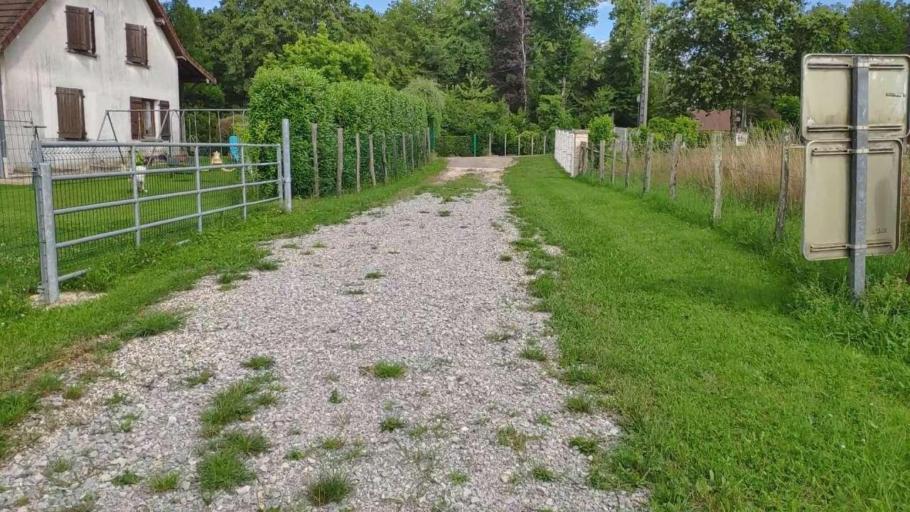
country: FR
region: Franche-Comte
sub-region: Departement du Jura
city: Bletterans
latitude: 46.7995
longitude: 5.4491
